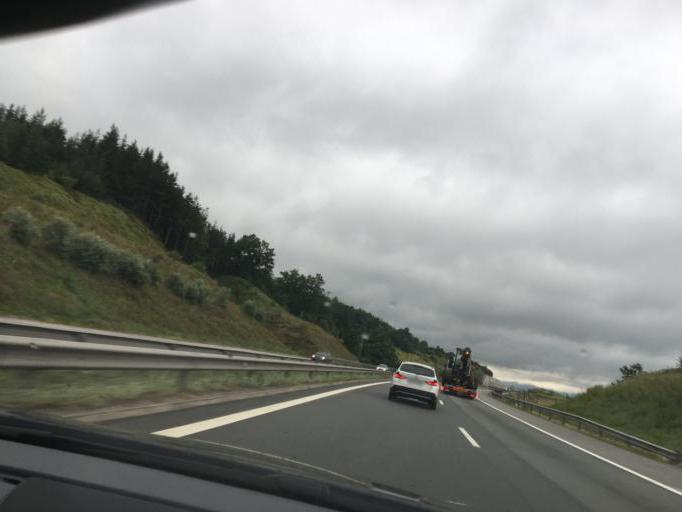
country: BG
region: Pernik
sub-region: Obshtina Pernik
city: Pernik
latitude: 42.6451
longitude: 23.1313
